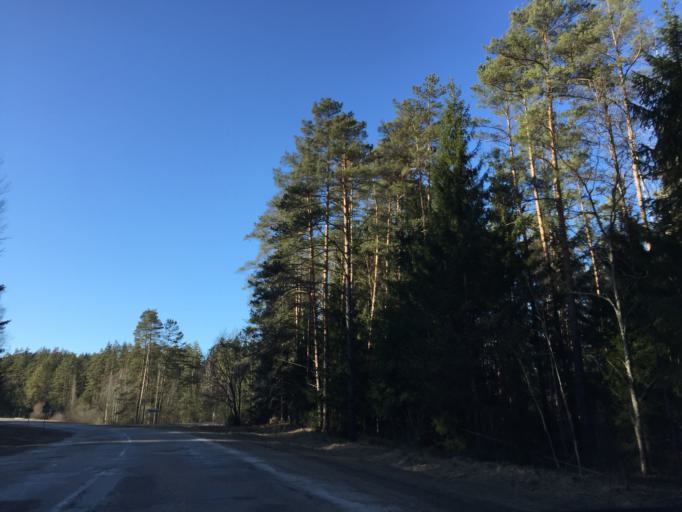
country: LV
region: Ropazu
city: Ropazi
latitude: 56.9486
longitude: 24.5946
